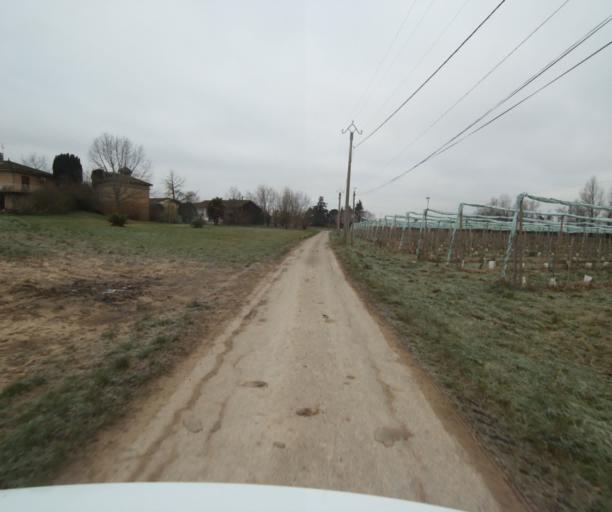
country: FR
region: Midi-Pyrenees
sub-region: Departement du Tarn-et-Garonne
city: Moissac
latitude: 44.1114
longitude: 1.1508
